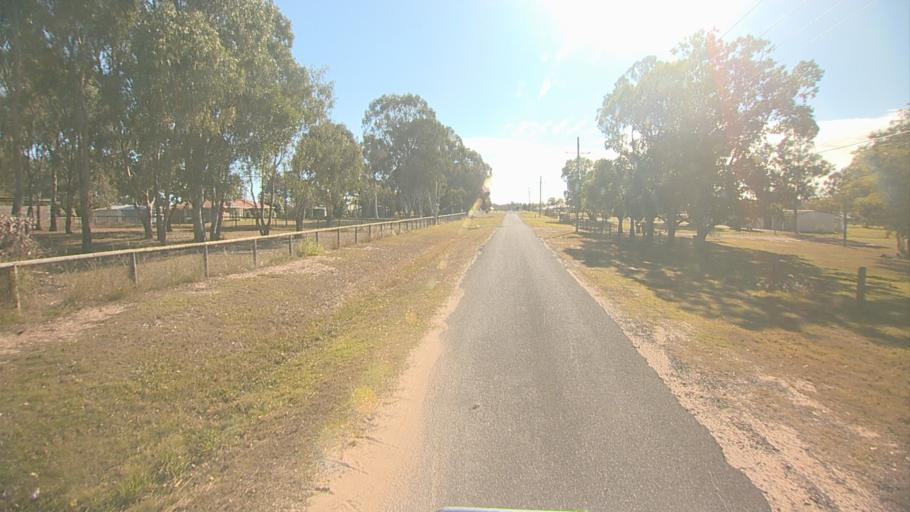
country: AU
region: Queensland
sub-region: Logan
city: Chambers Flat
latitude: -27.7763
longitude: 153.0898
